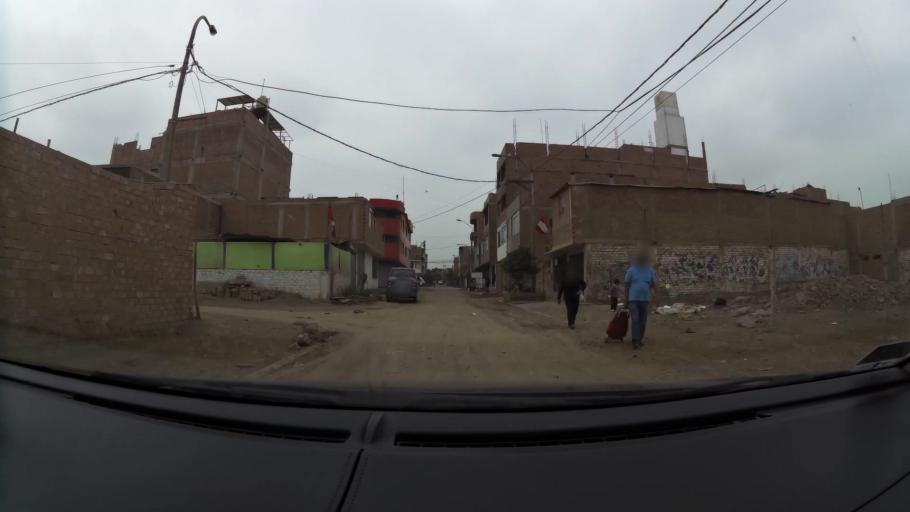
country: PE
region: Lima
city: Ventanilla
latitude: -11.9257
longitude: -77.0823
